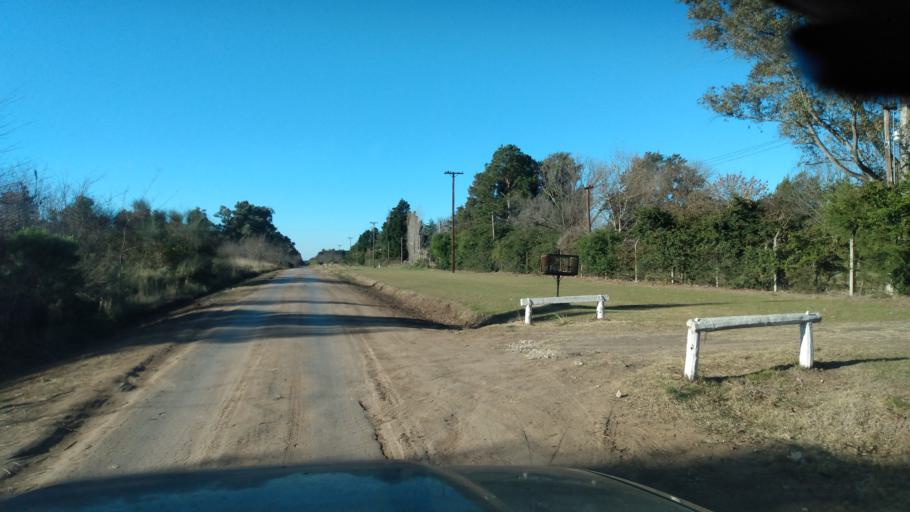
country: AR
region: Buenos Aires
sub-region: Partido de Lujan
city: Lujan
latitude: -34.5607
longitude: -59.1611
